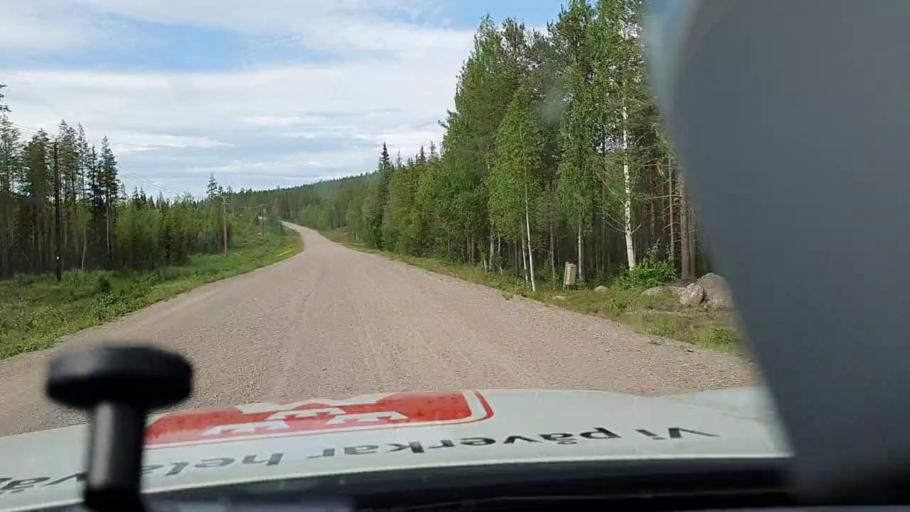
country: SE
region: Norrbotten
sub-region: Alvsbyns Kommun
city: AElvsbyn
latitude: 66.1261
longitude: 20.9962
